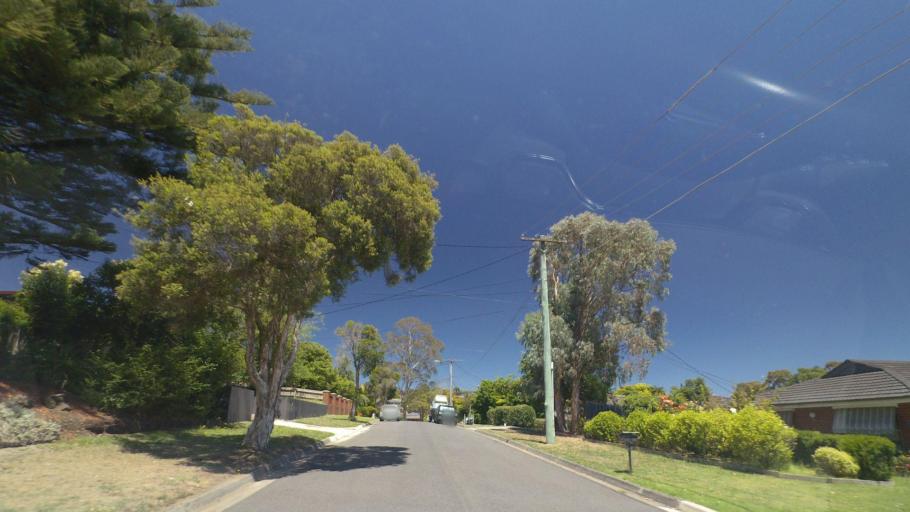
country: AU
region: Victoria
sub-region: Yarra Ranges
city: Lilydale
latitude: -37.7547
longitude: 145.3317
